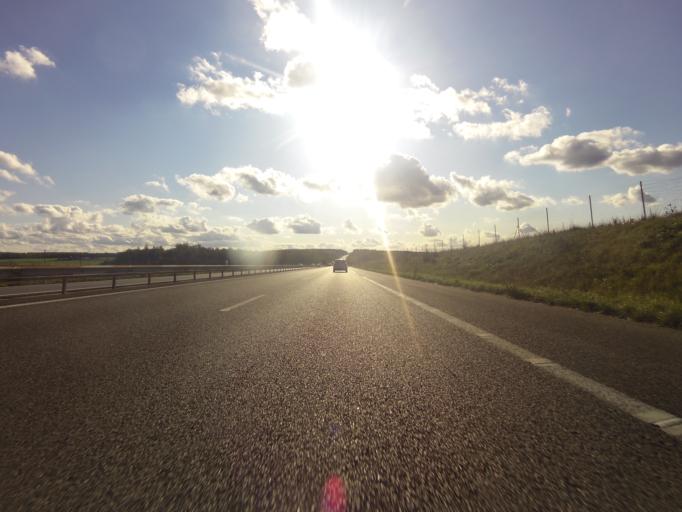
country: FR
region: Nord-Pas-de-Calais
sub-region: Departement du Pas-de-Calais
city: Hermies
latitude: 50.1093
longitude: 3.0717
